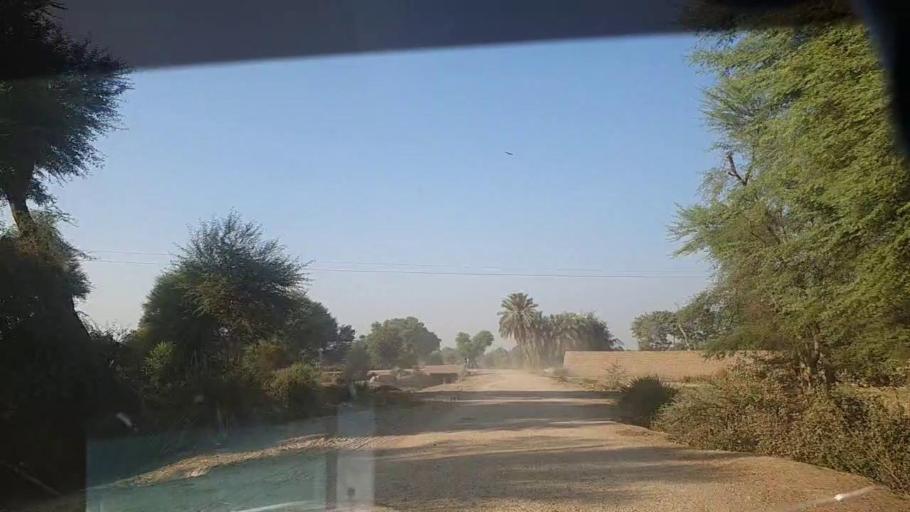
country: PK
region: Sindh
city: Sobhadero
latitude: 27.2690
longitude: 68.3477
